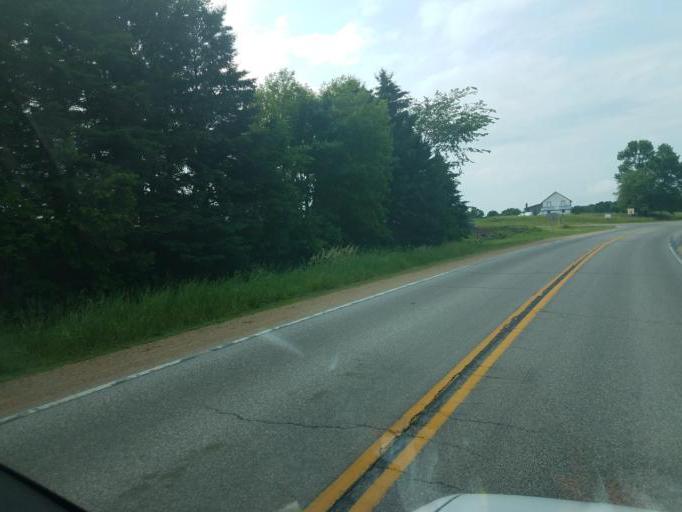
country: US
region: Wisconsin
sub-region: Vernon County
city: Hillsboro
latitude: 43.6194
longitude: -90.4522
